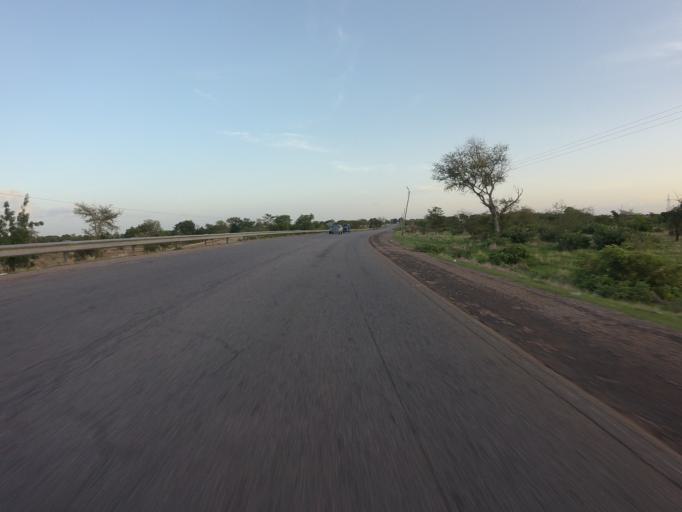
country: GH
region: Upper East
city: Navrongo
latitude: 10.9318
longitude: -1.0887
